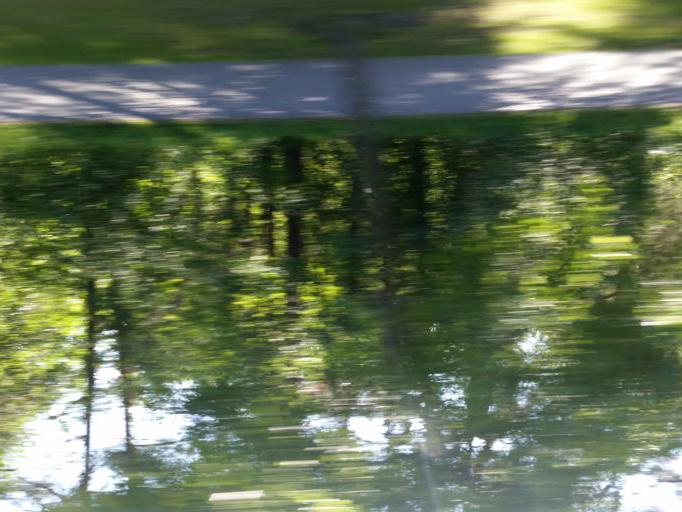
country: FI
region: Northern Savo
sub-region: Kuopio
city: Kuopio
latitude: 62.9008
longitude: 27.6754
